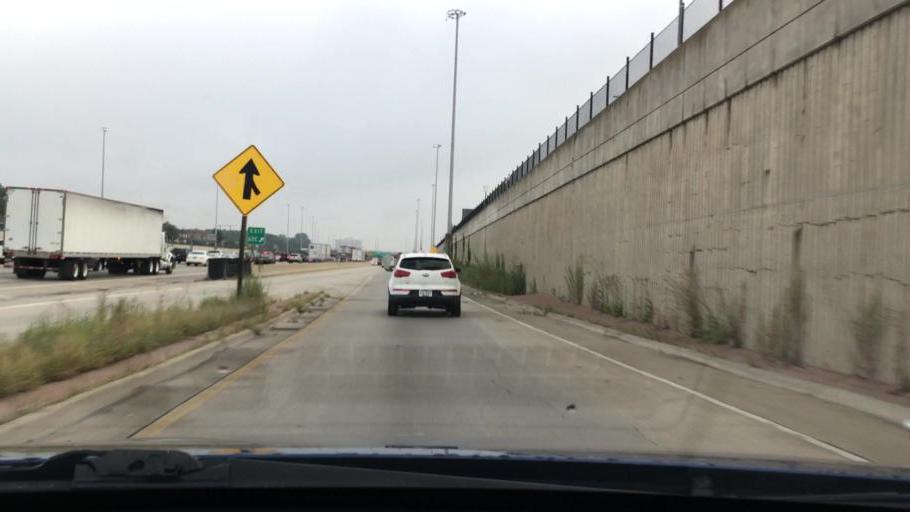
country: US
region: Illinois
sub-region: Cook County
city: Evergreen Park
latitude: 41.7456
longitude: -87.6245
